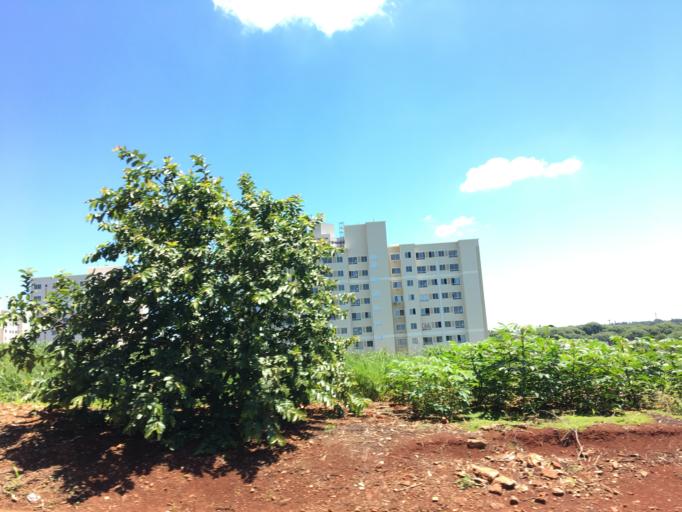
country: BR
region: Parana
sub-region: Maringa
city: Maringa
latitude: -23.4477
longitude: -51.9792
